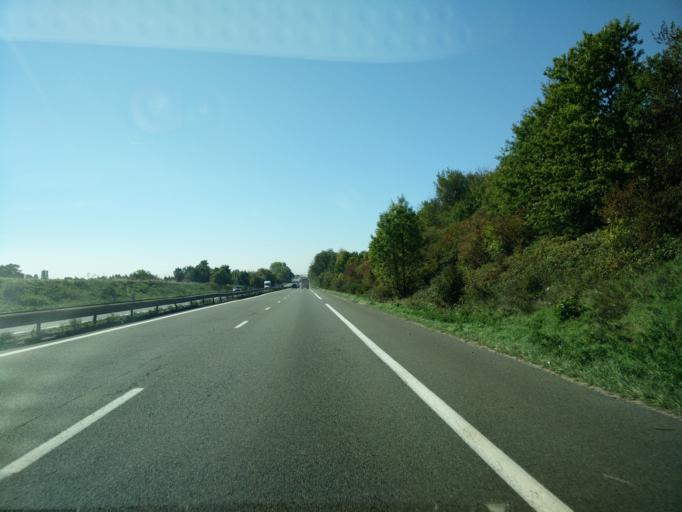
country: FR
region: Ile-de-France
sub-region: Departement de Seine-et-Marne
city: Mitry-Mory
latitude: 48.9916
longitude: 2.6192
